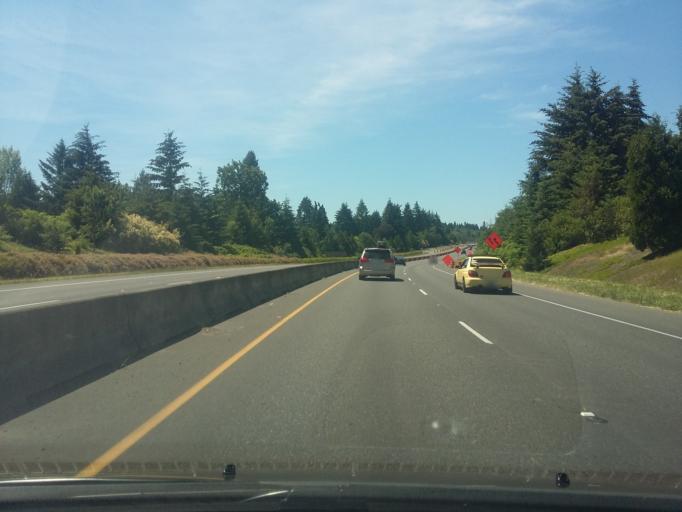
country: US
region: Washington
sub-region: Clark County
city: Five Corners
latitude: 45.6820
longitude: -122.5667
